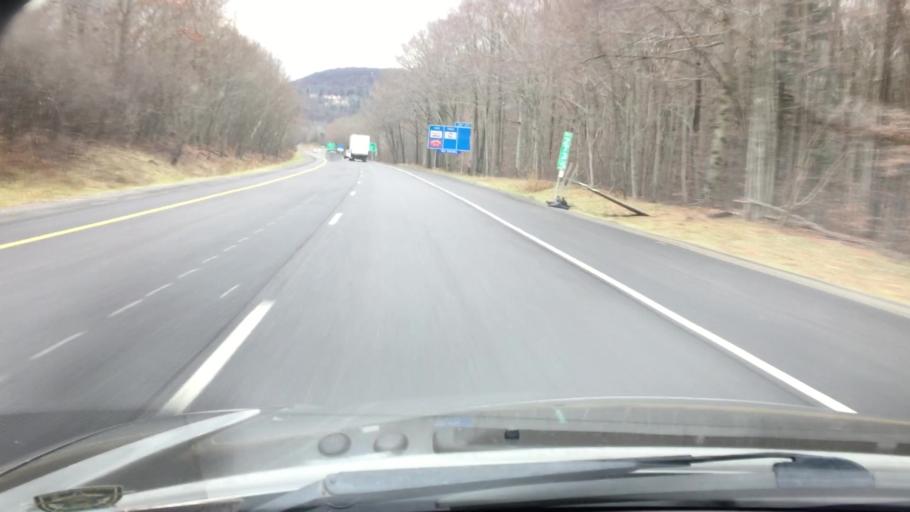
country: US
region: Pennsylvania
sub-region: Luzerne County
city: White Haven
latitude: 41.0595
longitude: -75.7582
